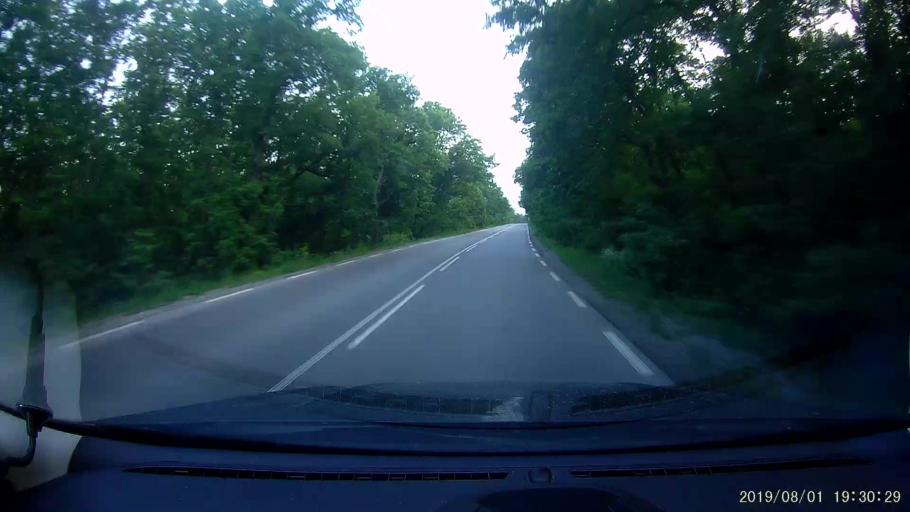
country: BG
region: Burgas
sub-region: Obshtina Sungurlare
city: Sungurlare
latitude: 42.8132
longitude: 26.8923
